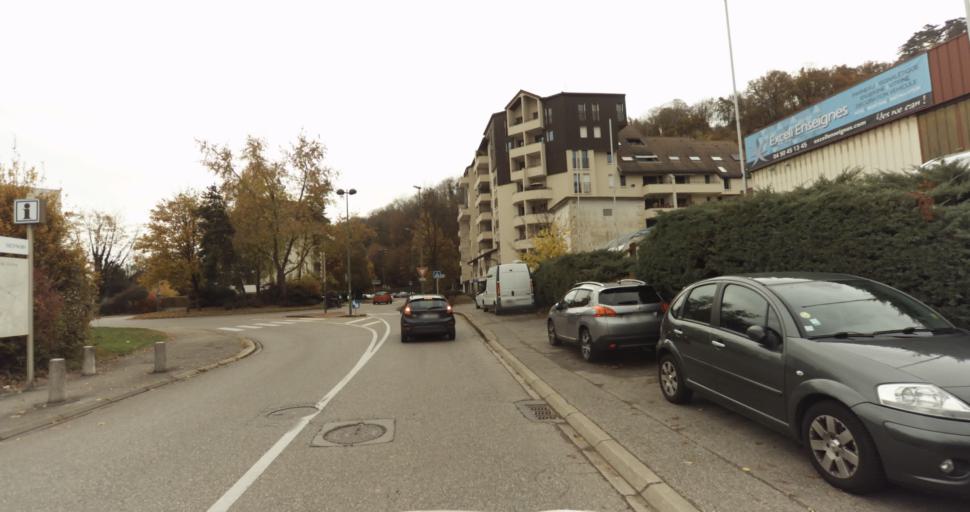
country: FR
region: Rhone-Alpes
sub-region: Departement de la Haute-Savoie
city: Annecy
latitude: 45.8897
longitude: 6.1231
